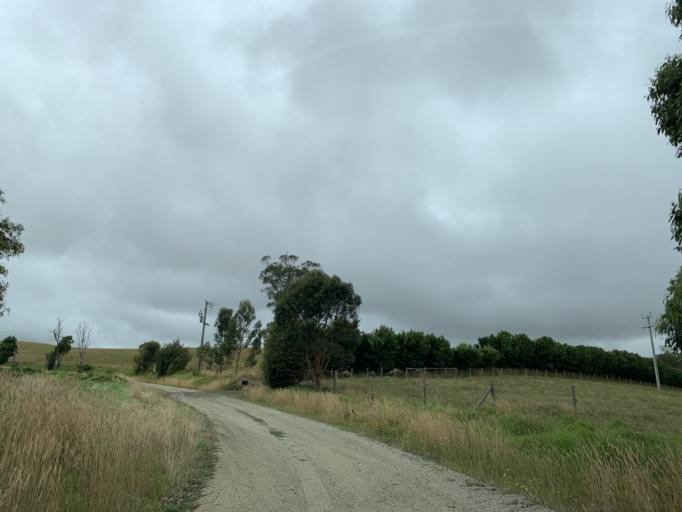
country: AU
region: Victoria
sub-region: Baw Baw
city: Warragul
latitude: -38.2879
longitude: 145.8774
